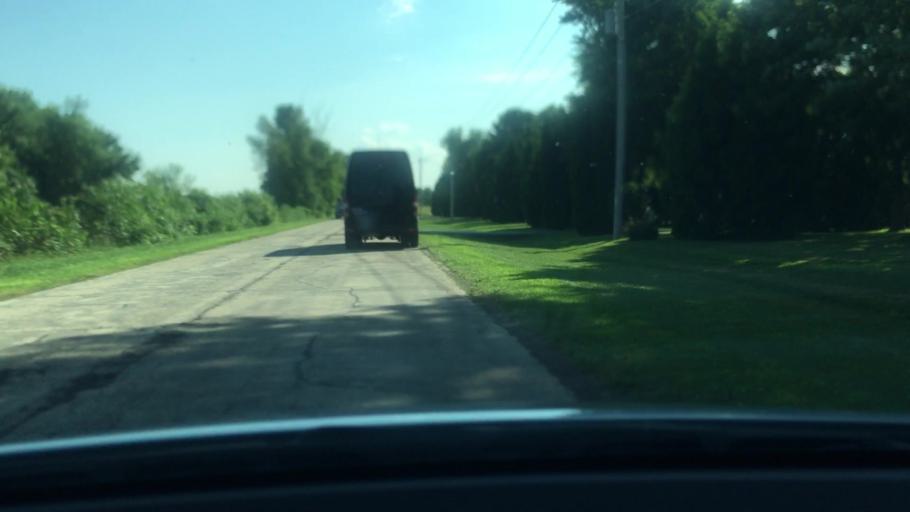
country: US
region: Wisconsin
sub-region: Winnebago County
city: Oshkosh
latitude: 43.9569
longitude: -88.5773
